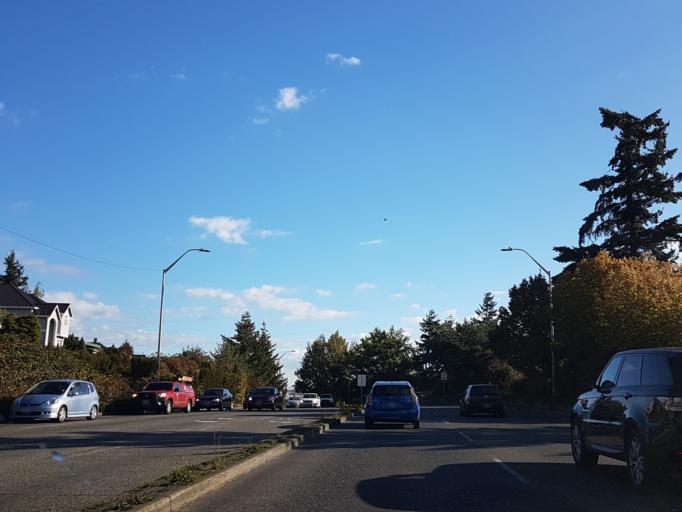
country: US
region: Washington
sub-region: King County
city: White Center
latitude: 47.5653
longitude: -122.3756
